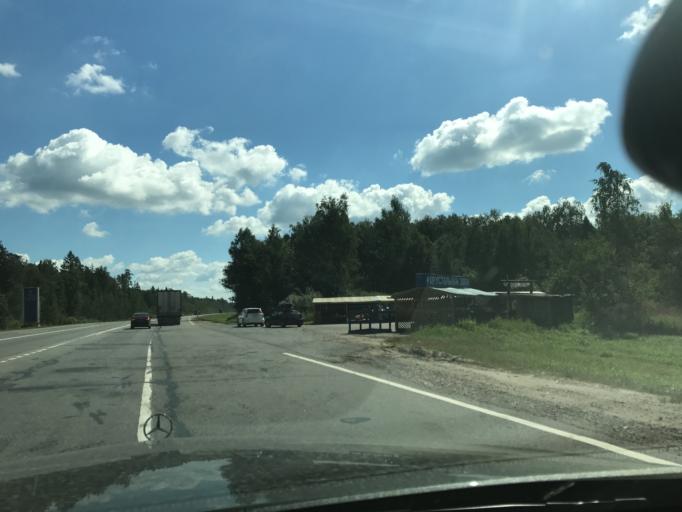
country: RU
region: Vladimir
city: Raduzhnyy
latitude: 56.0719
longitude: 40.2799
